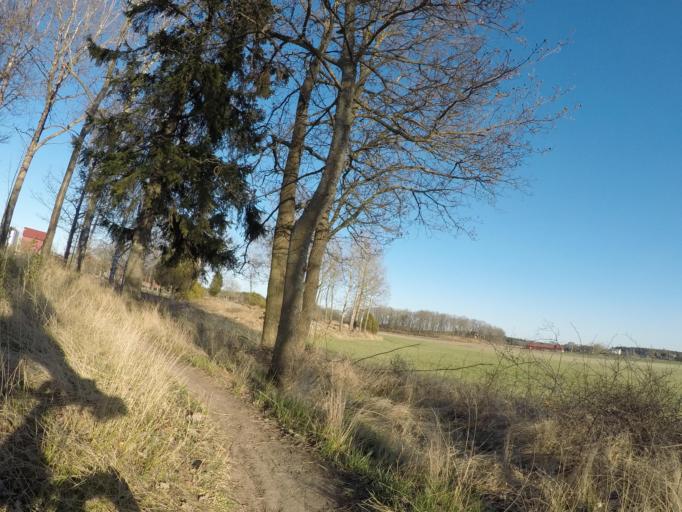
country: SE
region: Soedermanland
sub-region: Eskilstuna Kommun
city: Eskilstuna
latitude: 59.4085
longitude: 16.5080
